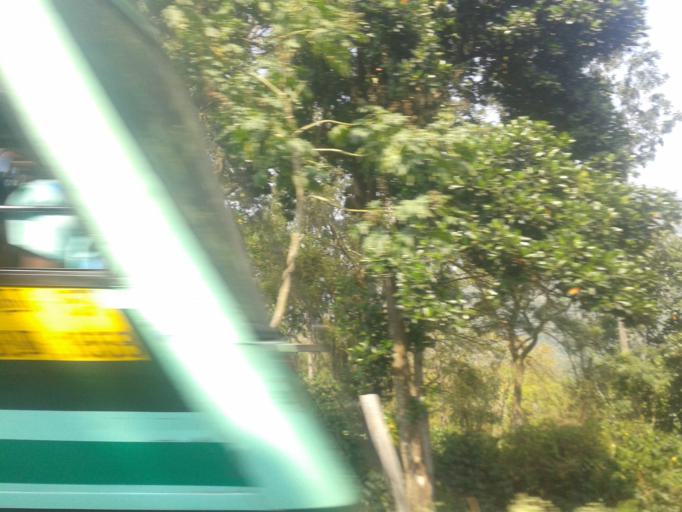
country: IN
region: Tamil Nadu
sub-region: Dindigul
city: Ayakudi
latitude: 10.3522
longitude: 77.5752
